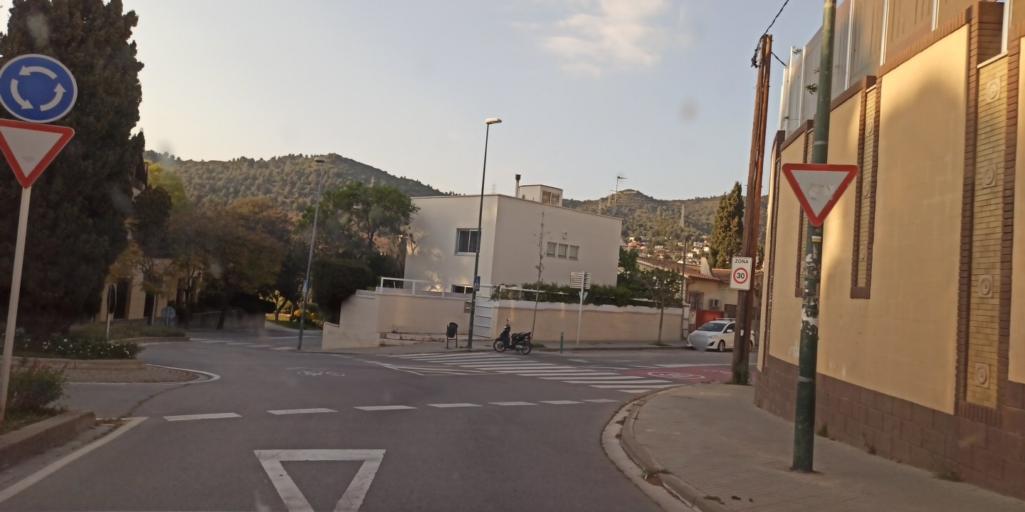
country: ES
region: Catalonia
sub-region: Provincia de Barcelona
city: Sant Just Desvern
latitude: 41.3866
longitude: 2.0734
